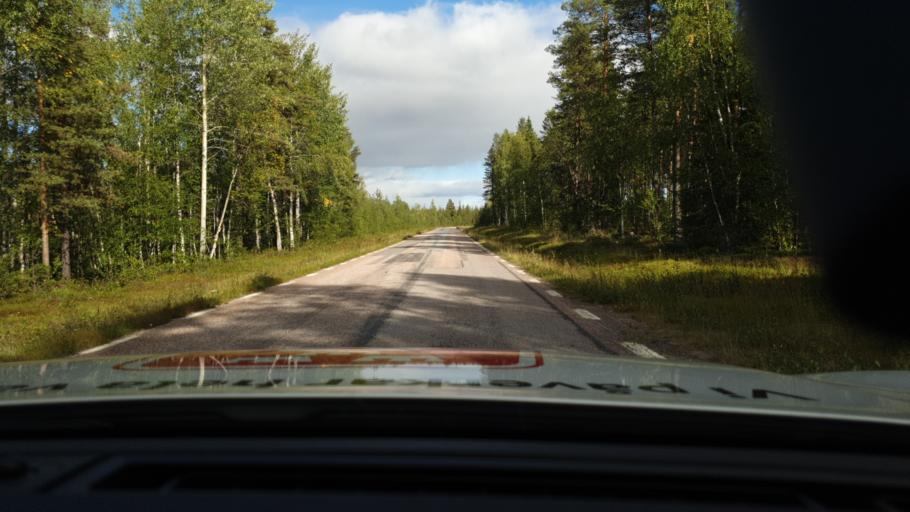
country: SE
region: Norrbotten
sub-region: Pajala Kommun
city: Pajala
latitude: 67.2523
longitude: 22.3343
